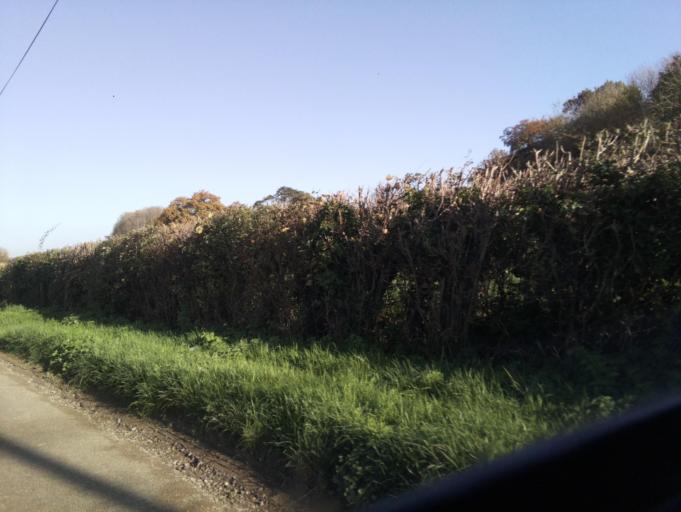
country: GB
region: England
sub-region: Somerset
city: Castle Cary
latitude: 51.0743
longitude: -2.4740
